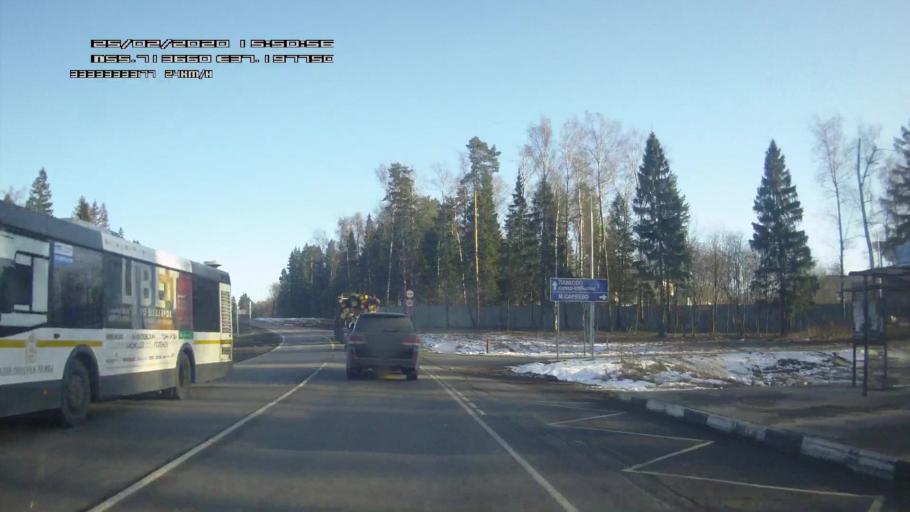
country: RU
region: Moskovskaya
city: Gorki Vtoryye
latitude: 55.7137
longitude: 37.1975
